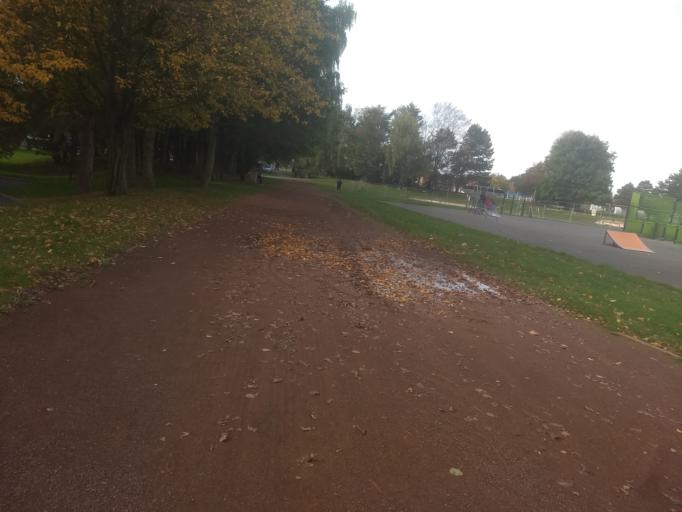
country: FR
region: Nord-Pas-de-Calais
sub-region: Departement du Pas-de-Calais
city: Dainville
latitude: 50.2841
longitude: 2.7307
